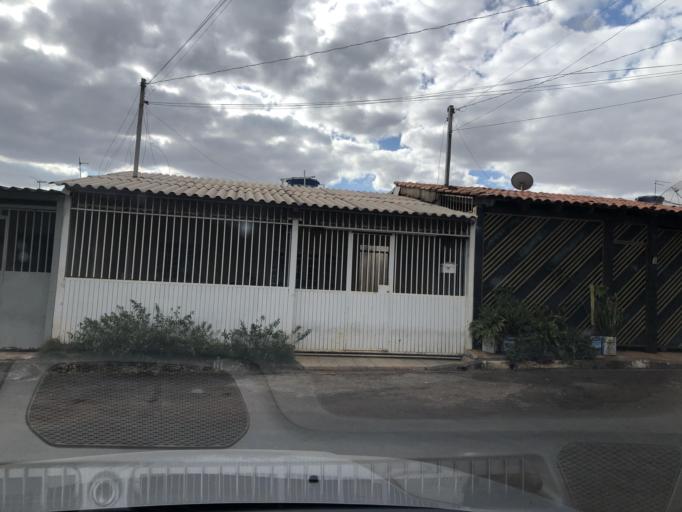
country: BR
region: Federal District
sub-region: Brasilia
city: Brasilia
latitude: -15.8918
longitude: -48.1192
